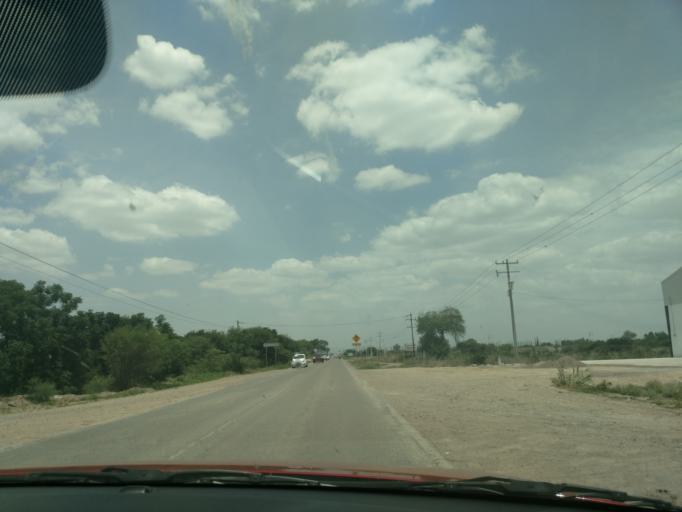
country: MX
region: San Luis Potosi
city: Ciudad Fernandez
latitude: 21.9445
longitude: -100.0486
